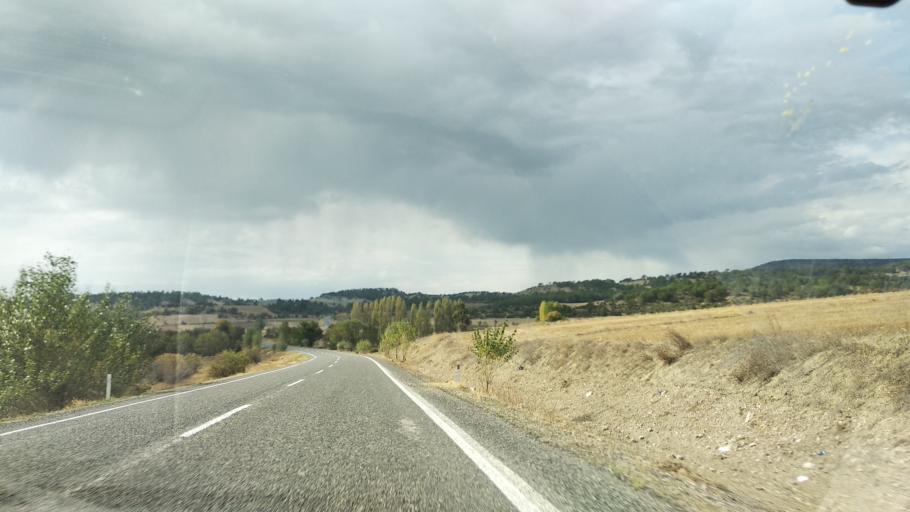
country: TR
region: Bolu
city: Seben
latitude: 40.3655
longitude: 31.4986
